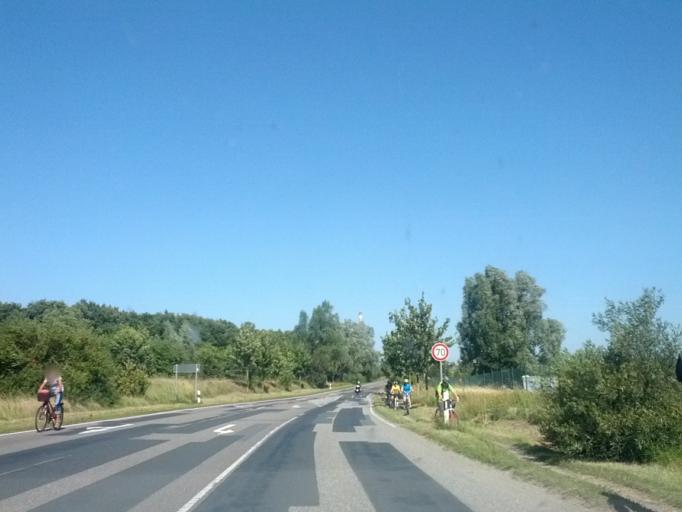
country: DE
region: Mecklenburg-Vorpommern
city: Sagard
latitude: 54.4841
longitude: 13.5778
